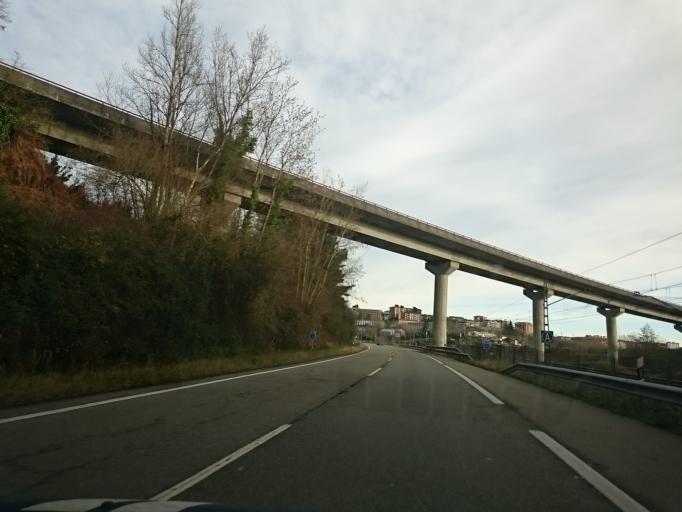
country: ES
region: Asturias
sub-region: Province of Asturias
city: Oviedo
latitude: 43.3469
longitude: -5.8600
